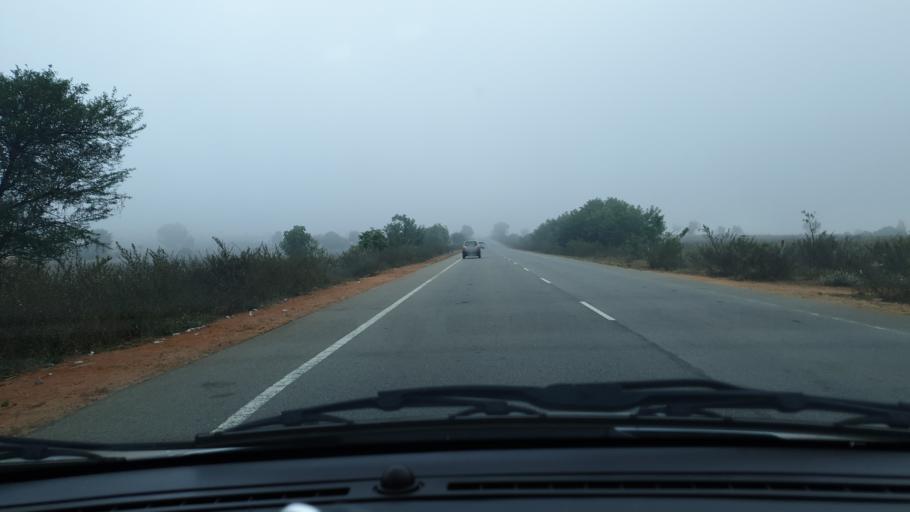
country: IN
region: Telangana
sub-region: Nalgonda
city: Devarkonda
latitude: 16.6310
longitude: 78.6501
